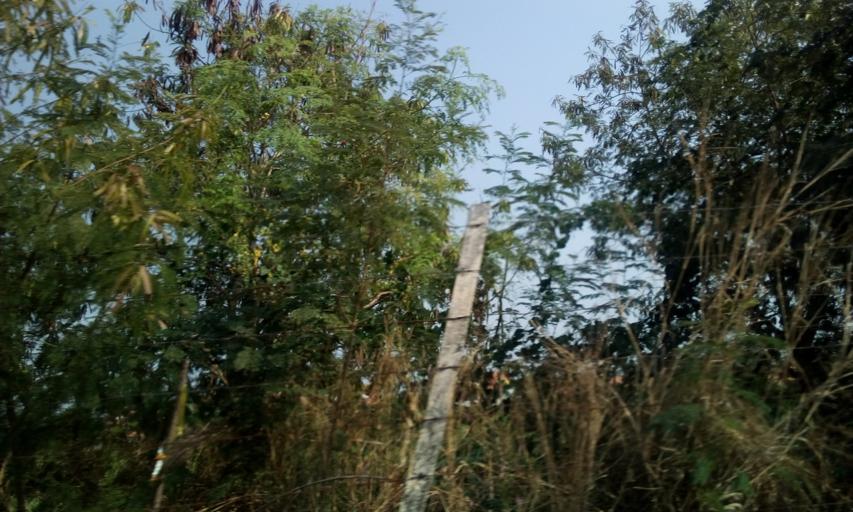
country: TH
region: Pathum Thani
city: Ban Rangsit
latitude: 14.0171
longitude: 100.7591
